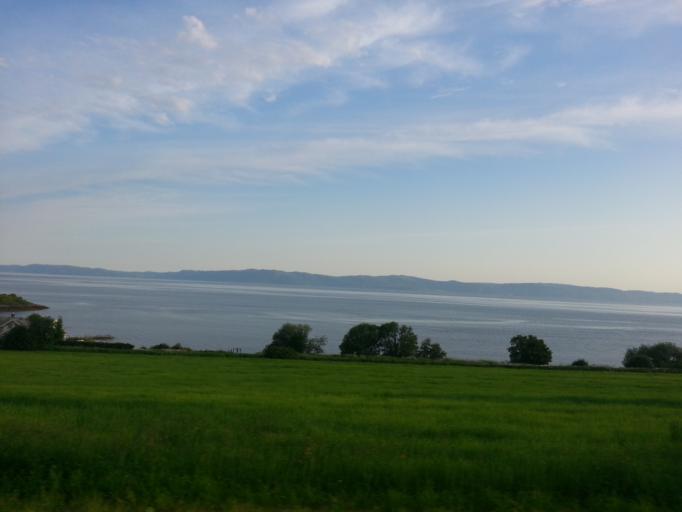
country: NO
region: Sor-Trondelag
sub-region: Malvik
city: Malvik
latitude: 63.4345
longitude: 10.5783
